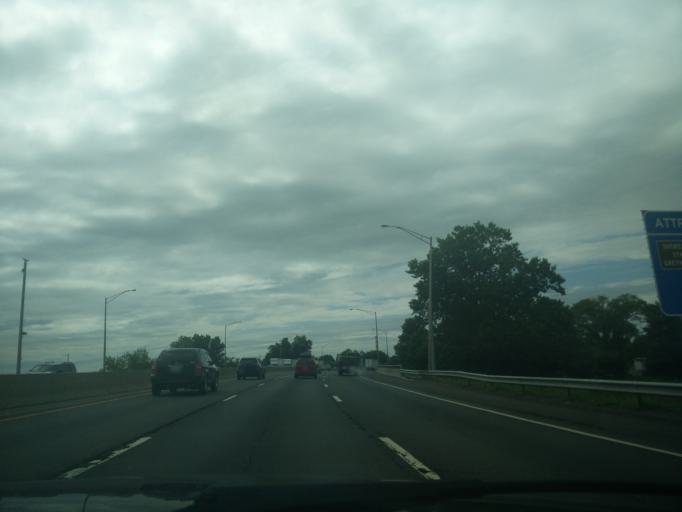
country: US
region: Connecticut
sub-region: Fairfield County
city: Stratford
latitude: 41.1752
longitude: -73.1532
